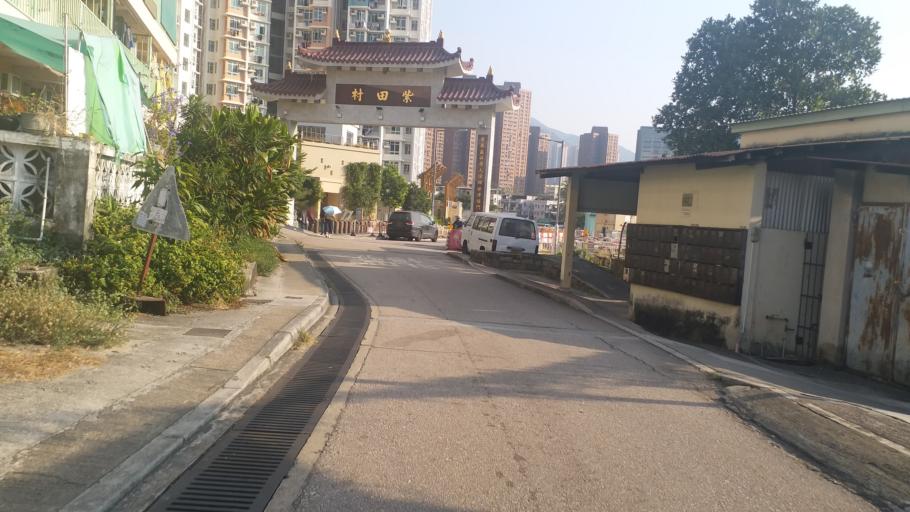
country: HK
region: Tuen Mun
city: Tuen Mun
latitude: 22.4151
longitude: 113.9743
